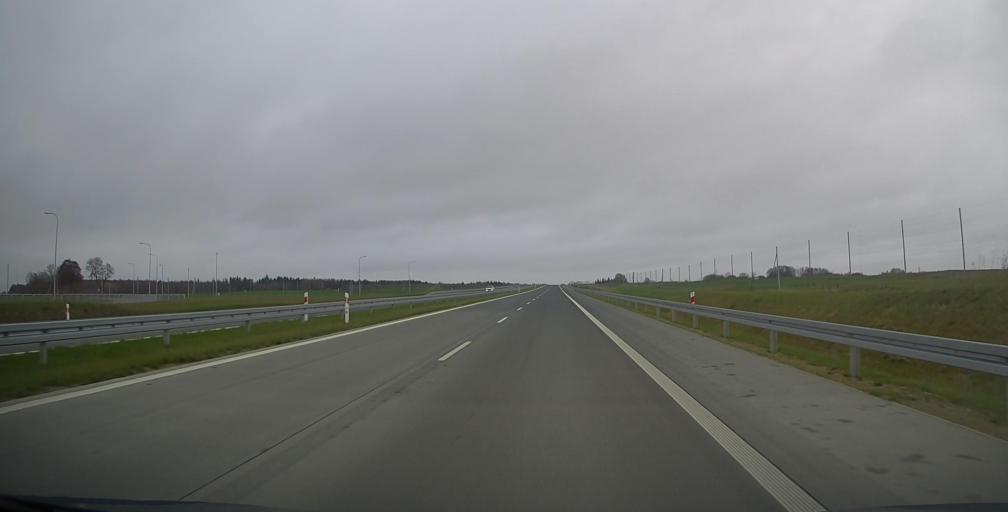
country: PL
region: Podlasie
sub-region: Powiat suwalski
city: Raczki
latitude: 53.8835
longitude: 22.6693
